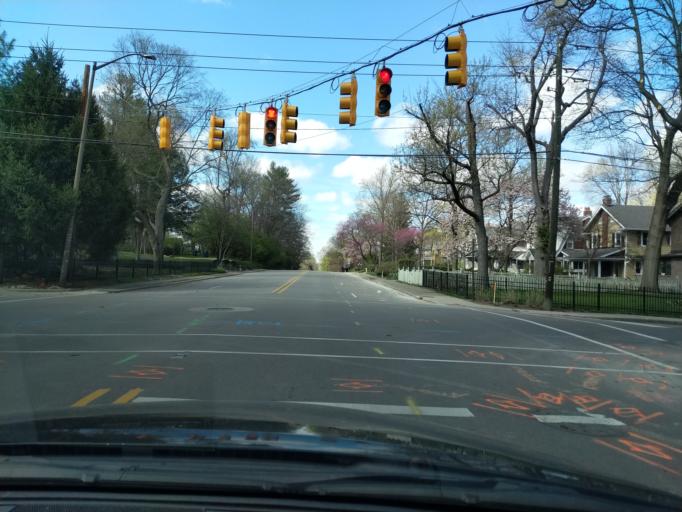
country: US
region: Indiana
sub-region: Marion County
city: Broad Ripple
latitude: 39.8541
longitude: -86.1501
